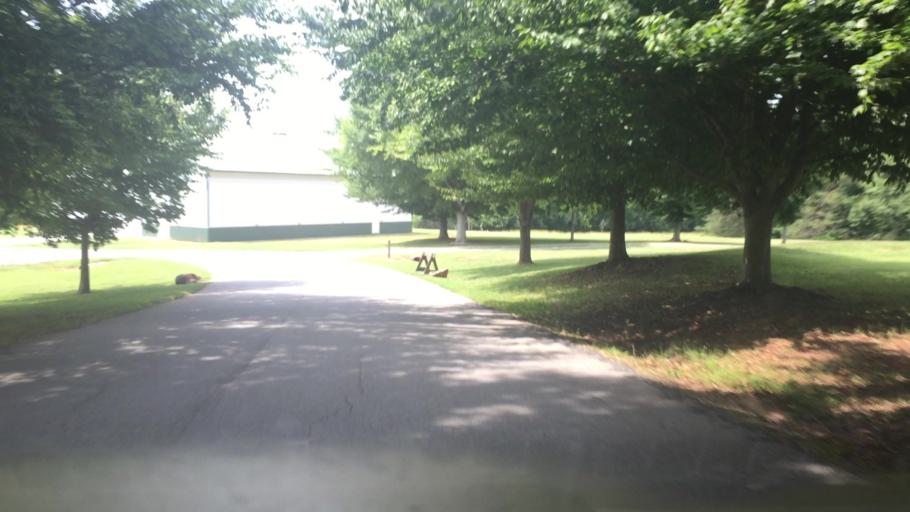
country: US
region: North Carolina
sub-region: Rowan County
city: China Grove
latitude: 35.6479
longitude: -80.6446
